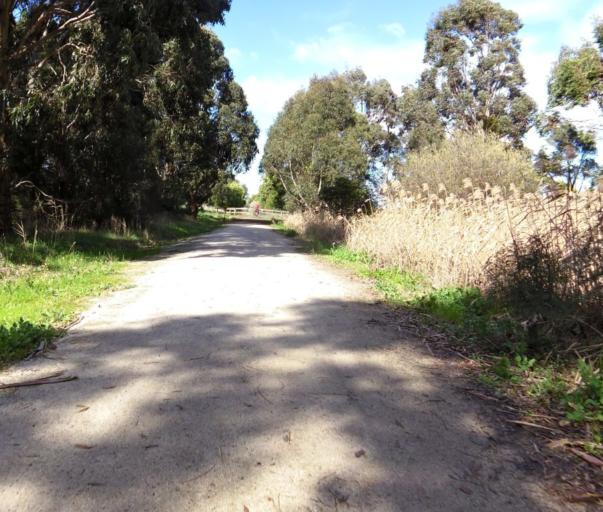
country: AU
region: Victoria
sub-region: Baw Baw
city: Warragul
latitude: -38.4959
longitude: 145.9404
